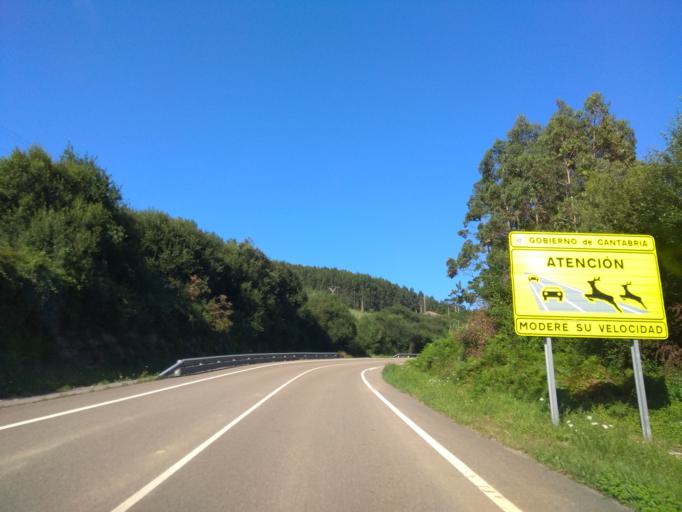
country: ES
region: Cantabria
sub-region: Provincia de Cantabria
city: Bareyo
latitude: 43.4720
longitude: -3.6525
